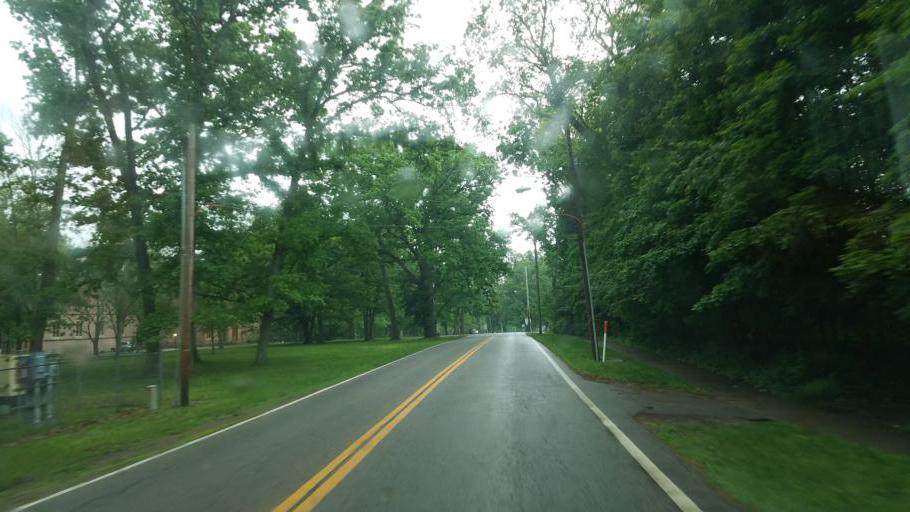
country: US
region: Ohio
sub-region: Knox County
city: Gambier
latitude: 40.3823
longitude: -82.3979
